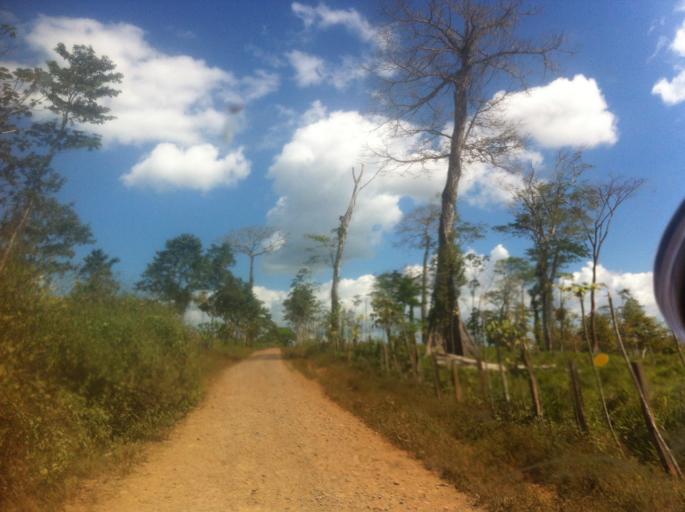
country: CR
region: Alajuela
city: Los Chiles
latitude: 11.2394
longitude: -84.4776
